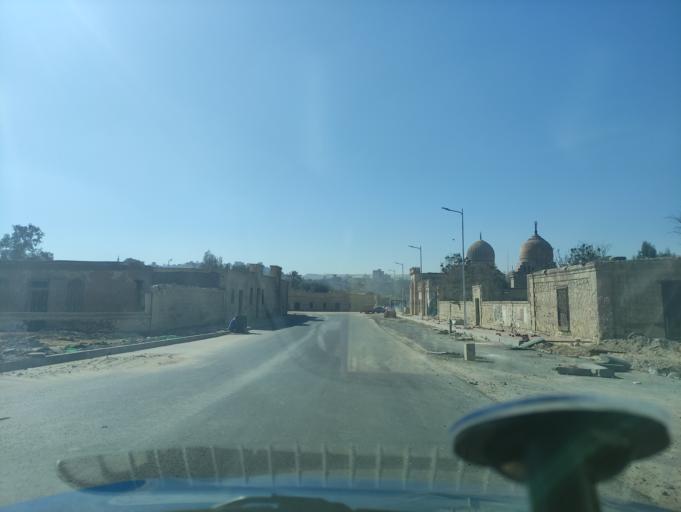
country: EG
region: Muhafazat al Qahirah
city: Cairo
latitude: 30.0538
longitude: 31.2802
